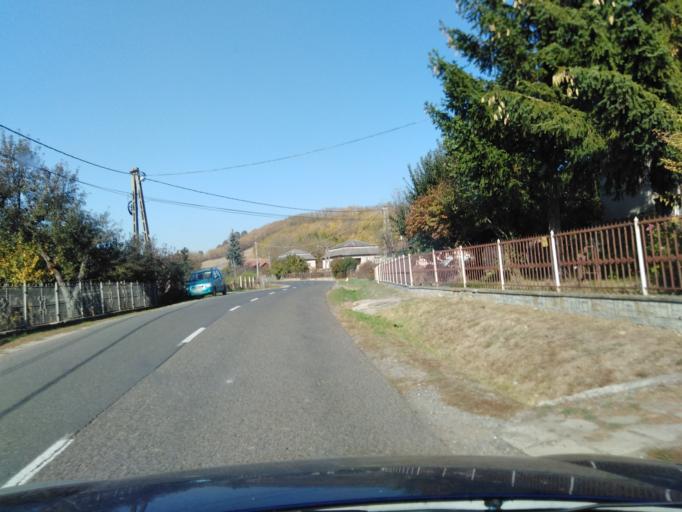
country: HU
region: Nograd
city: Karancskeszi
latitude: 48.1697
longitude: 19.6923
